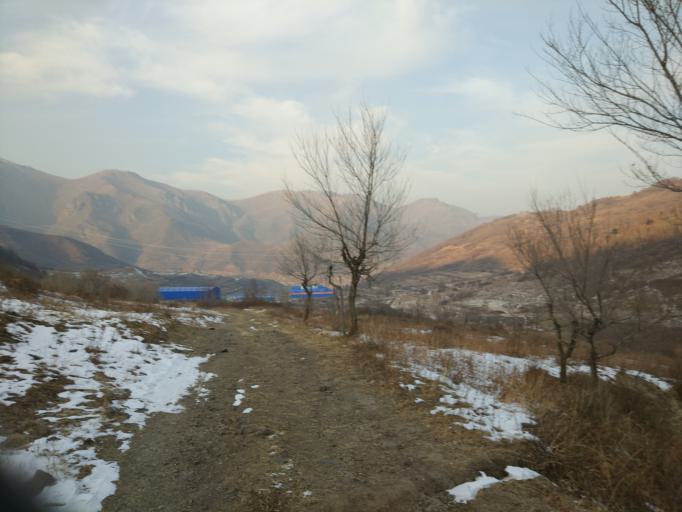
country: CN
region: Hebei
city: Xiwanzi
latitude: 40.8013
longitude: 115.4586
